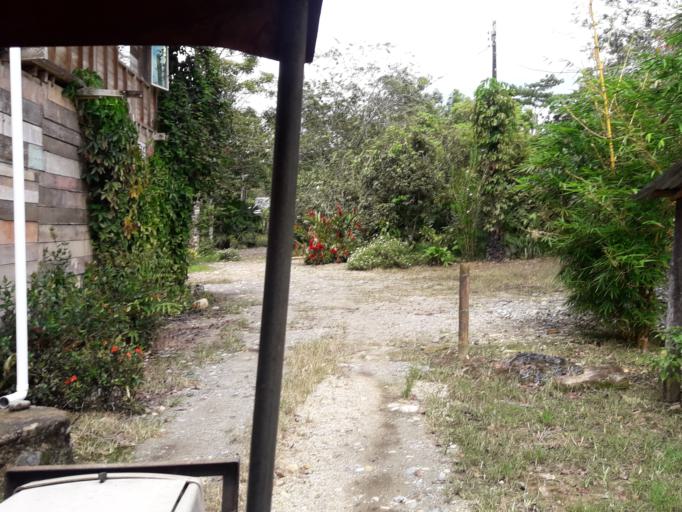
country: EC
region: Napo
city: Tena
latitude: -1.0717
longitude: -77.7957
